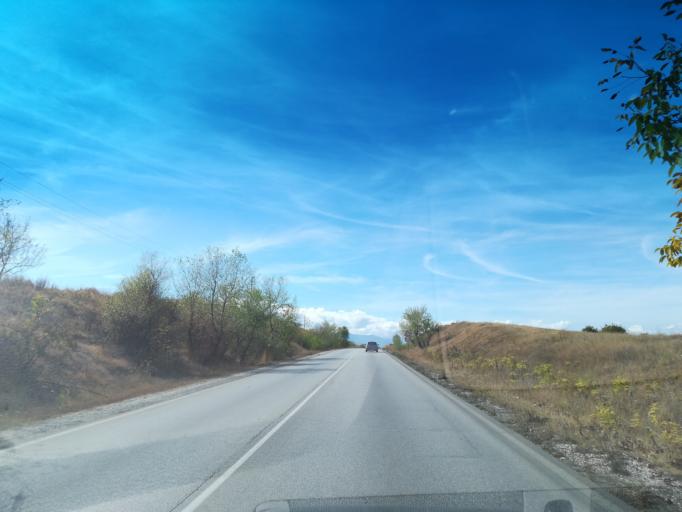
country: BG
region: Plovdiv
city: Stamboliyski
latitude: 42.1308
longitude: 24.6054
